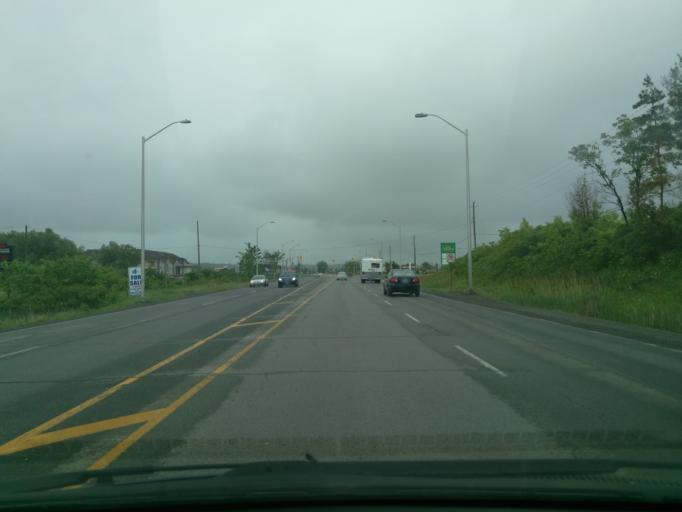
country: CA
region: Ontario
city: Clarence-Rockland
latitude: 45.5491
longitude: -75.2986
